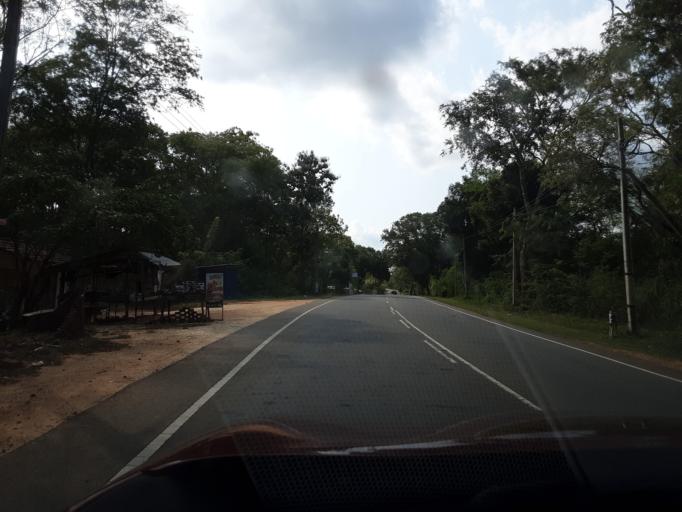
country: LK
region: Uva
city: Haputale
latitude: 6.3668
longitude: 81.1756
